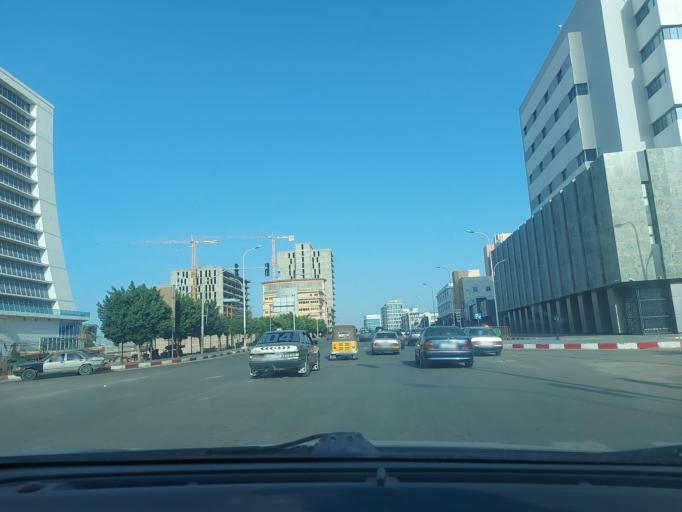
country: MR
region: Nouakchott
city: Nouakchott
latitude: 18.0875
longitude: -15.9747
